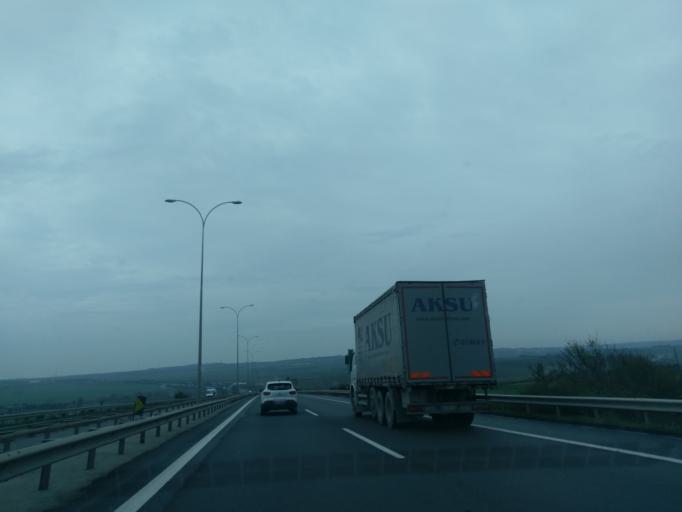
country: TR
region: Istanbul
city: Silivri
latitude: 41.1154
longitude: 28.2579
